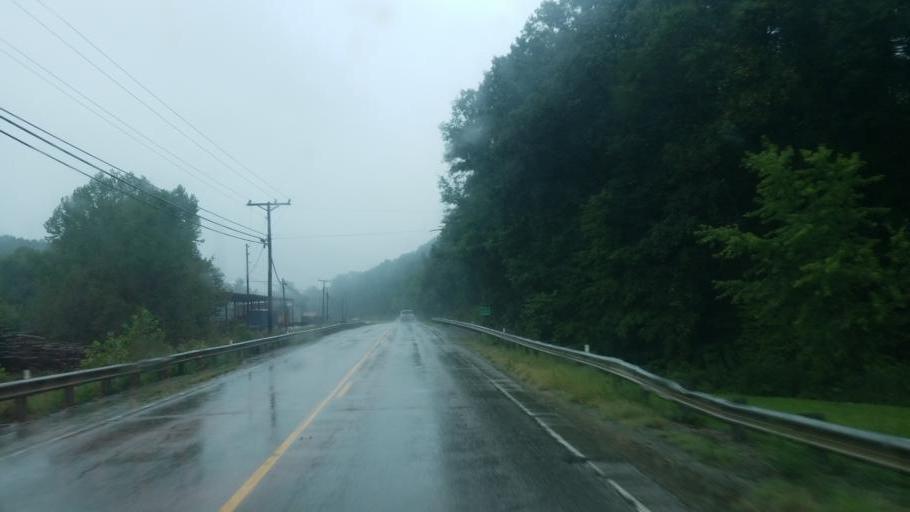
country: US
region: Kentucky
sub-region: Rowan County
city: Morehead
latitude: 38.2231
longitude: -83.4883
